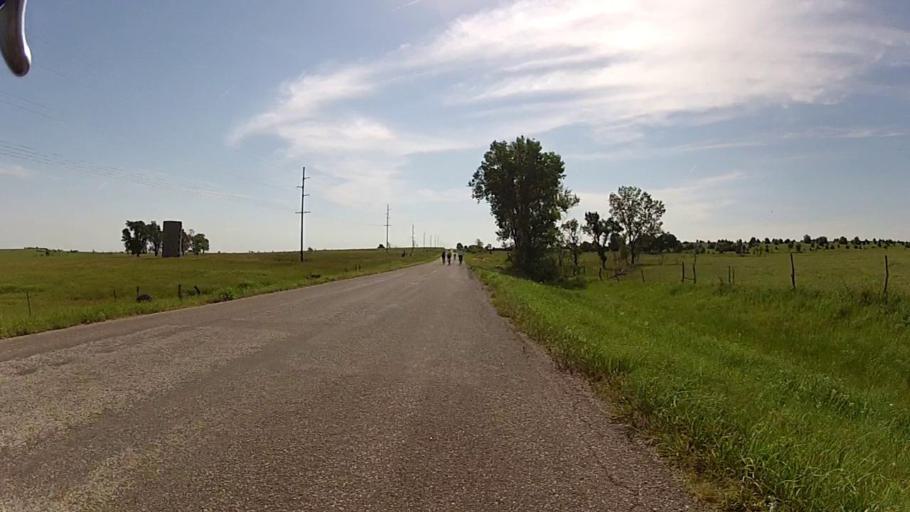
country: US
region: Kansas
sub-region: Cowley County
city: Winfield
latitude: 37.0710
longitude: -96.6546
